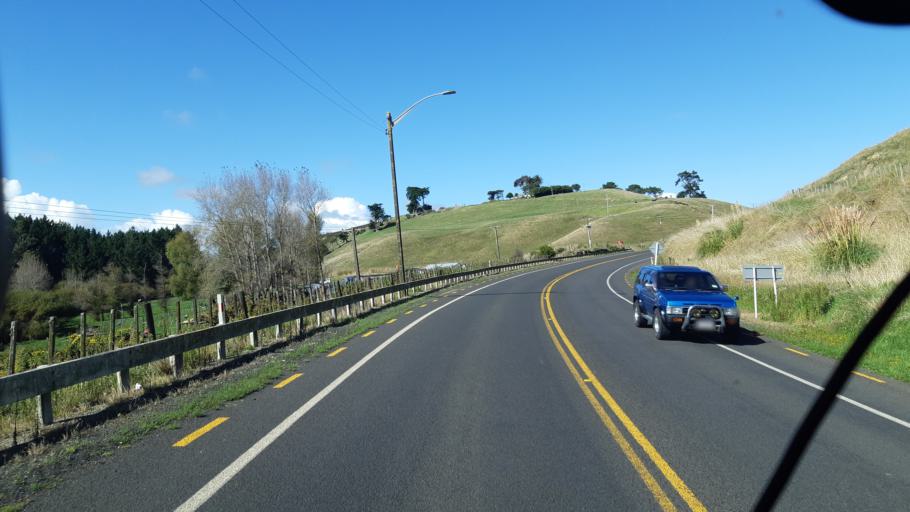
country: NZ
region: Manawatu-Wanganui
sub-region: Wanganui District
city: Wanganui
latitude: -39.9614
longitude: 175.0989
